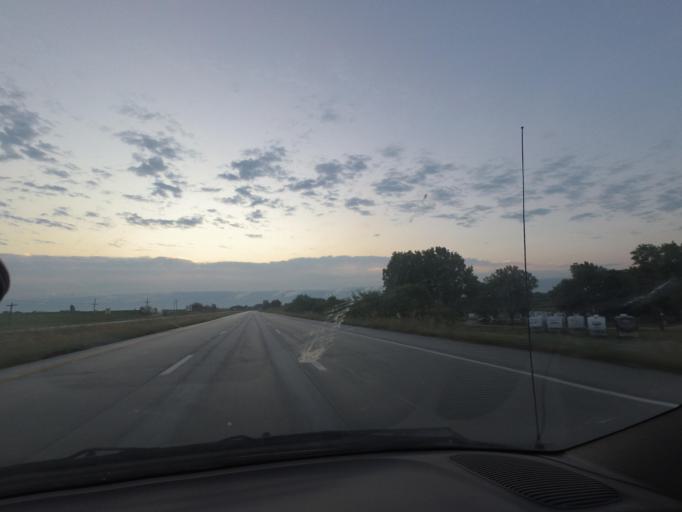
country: US
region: Missouri
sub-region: Macon County
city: Macon
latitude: 39.7601
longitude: -92.5593
